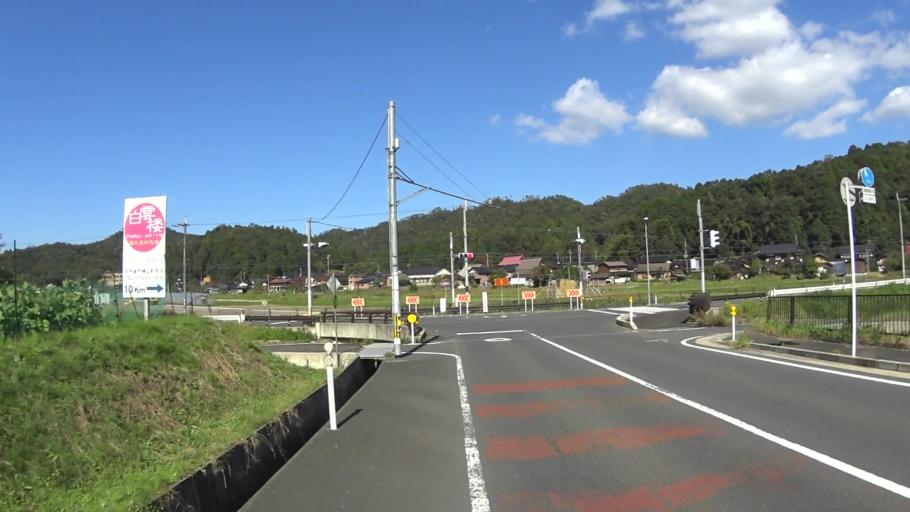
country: JP
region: Hyogo
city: Toyooka
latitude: 35.5732
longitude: 134.9782
